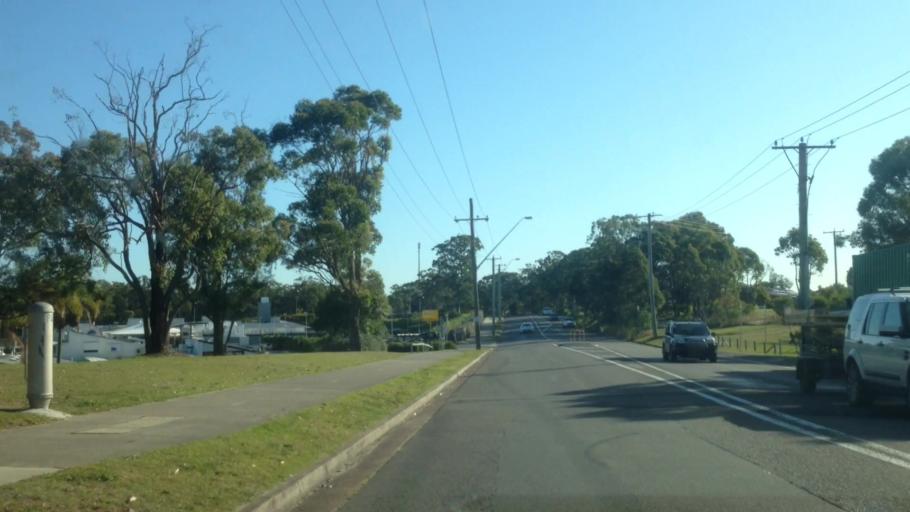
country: AU
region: New South Wales
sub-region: Lake Macquarie Shire
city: Dora Creek
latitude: -33.1092
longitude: 151.5339
